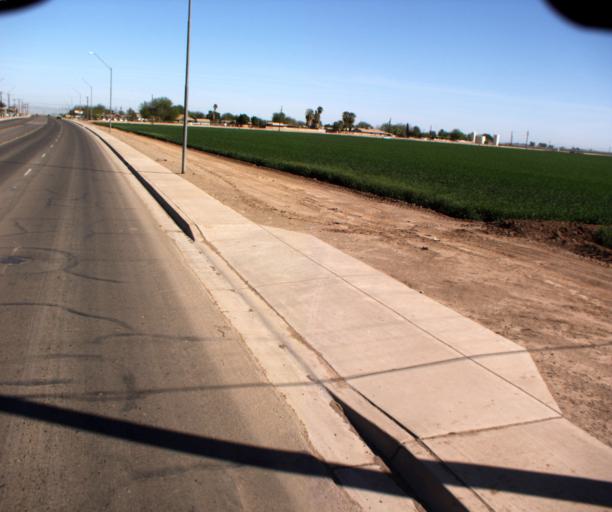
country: US
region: Arizona
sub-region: Yuma County
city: San Luis
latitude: 32.5573
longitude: -114.7847
